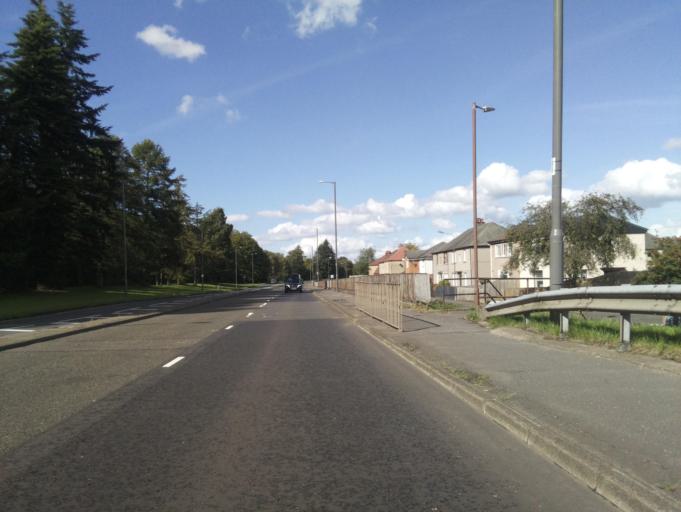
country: GB
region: Scotland
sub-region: Stirling
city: Stirling
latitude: 56.1086
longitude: -3.9321
